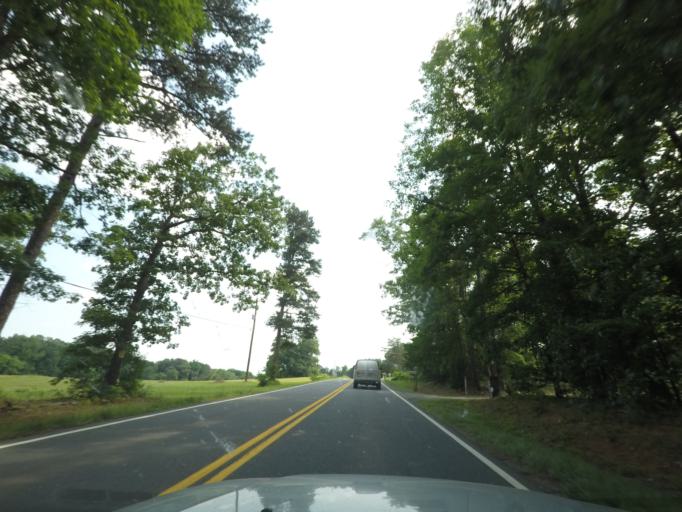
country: US
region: Virginia
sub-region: Fluvanna County
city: Palmyra
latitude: 37.9098
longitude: -78.2565
